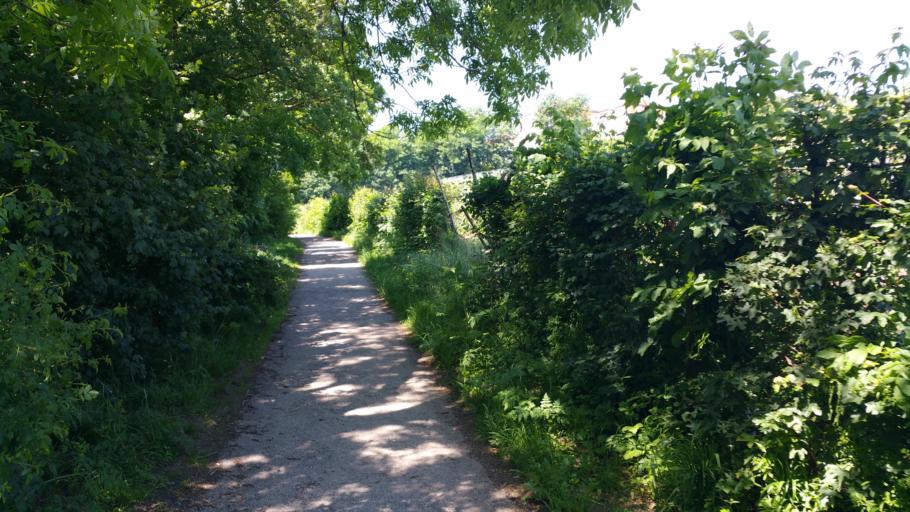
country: AT
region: Vienna
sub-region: Wien Stadt
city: Vienna
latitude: 48.2188
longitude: 16.2895
